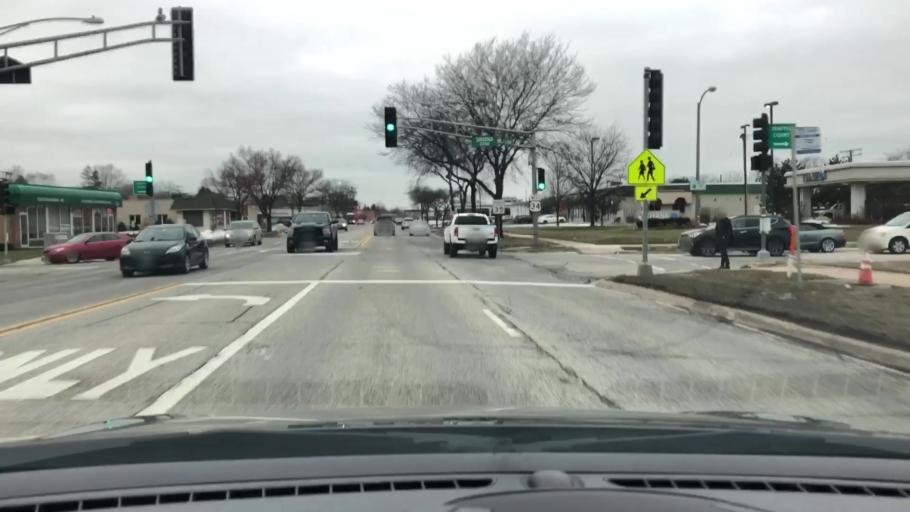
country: US
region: Illinois
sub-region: DuPage County
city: Downers Grove
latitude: 41.8086
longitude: -88.0145
